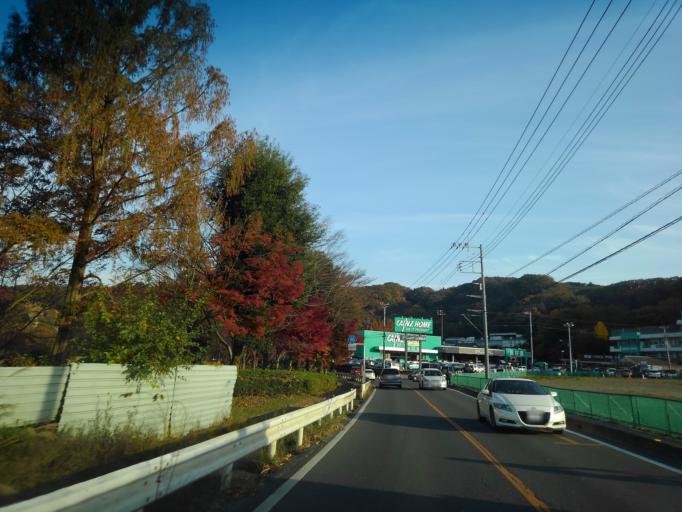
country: JP
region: Saitama
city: Hanno
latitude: 35.8324
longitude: 139.3392
